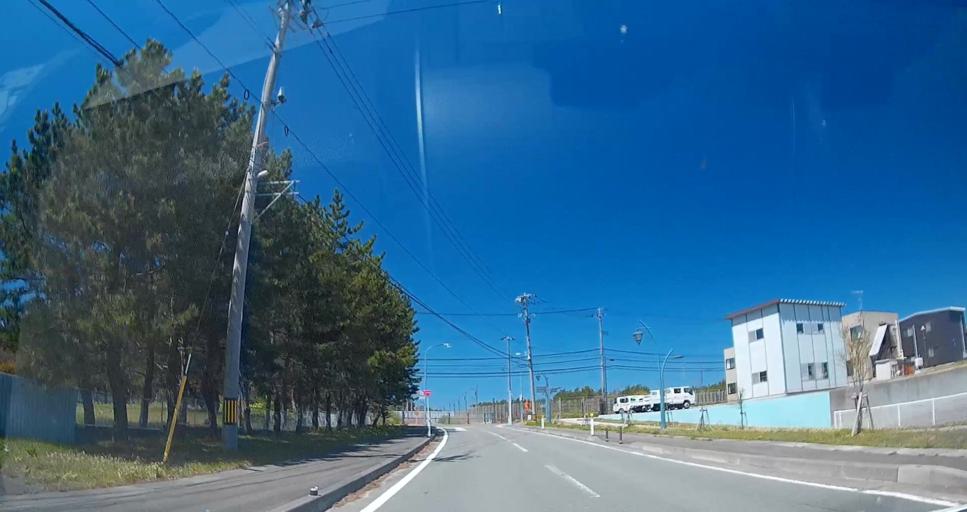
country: JP
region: Aomori
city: Misawa
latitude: 40.9700
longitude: 141.3604
